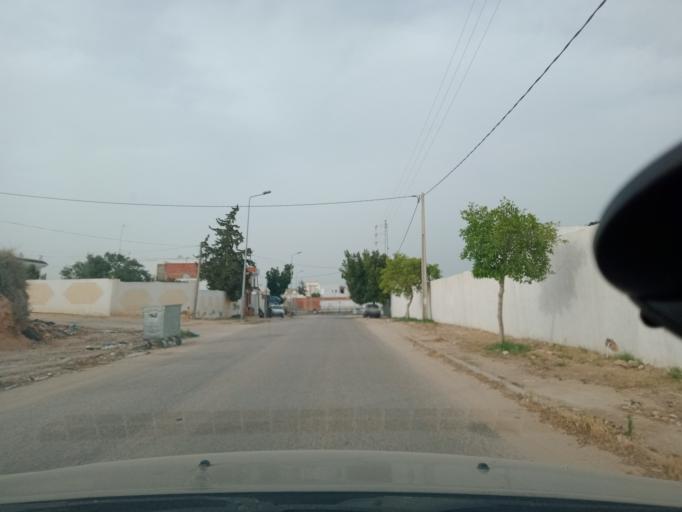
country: TN
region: Safaqis
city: Al Qarmadah
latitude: 34.7924
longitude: 10.7734
